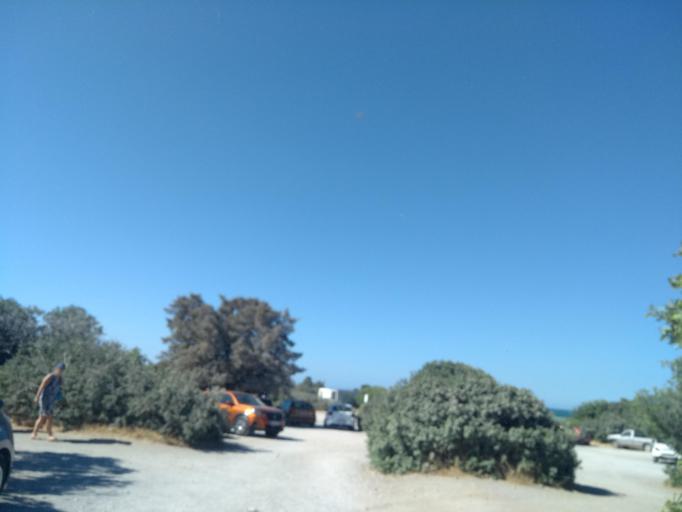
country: GR
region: Crete
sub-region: Nomos Chanias
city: Palaiochora
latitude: 35.2724
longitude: 23.5436
